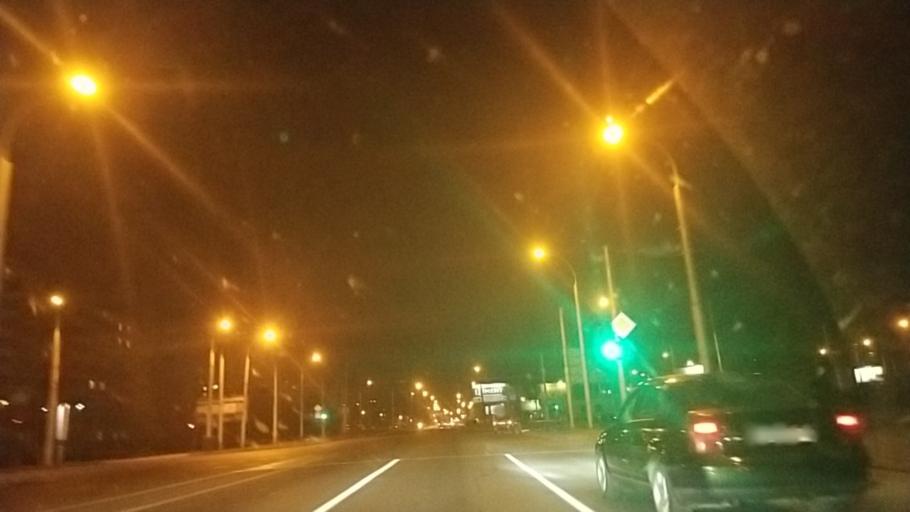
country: BY
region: Brest
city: Brest
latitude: 52.0706
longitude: 23.7491
